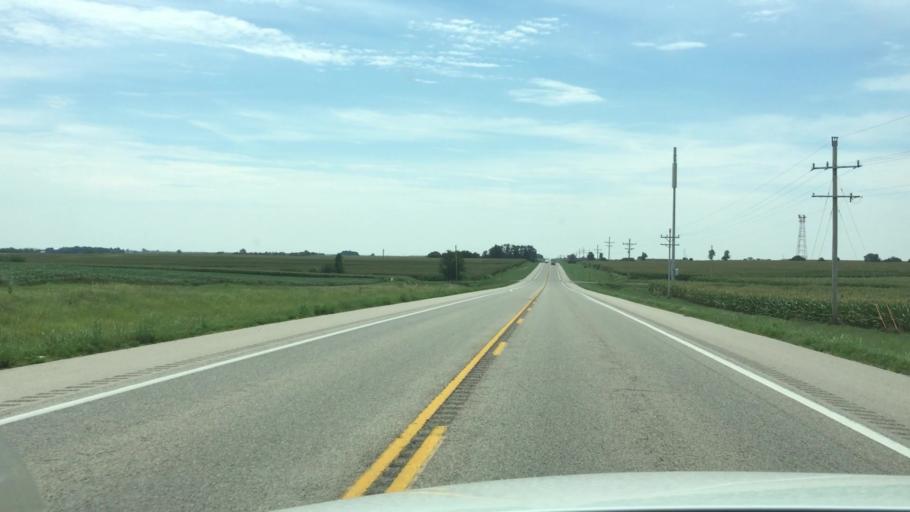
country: US
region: Kansas
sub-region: Nemaha County
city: Sabetha
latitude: 39.7709
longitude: -95.7296
